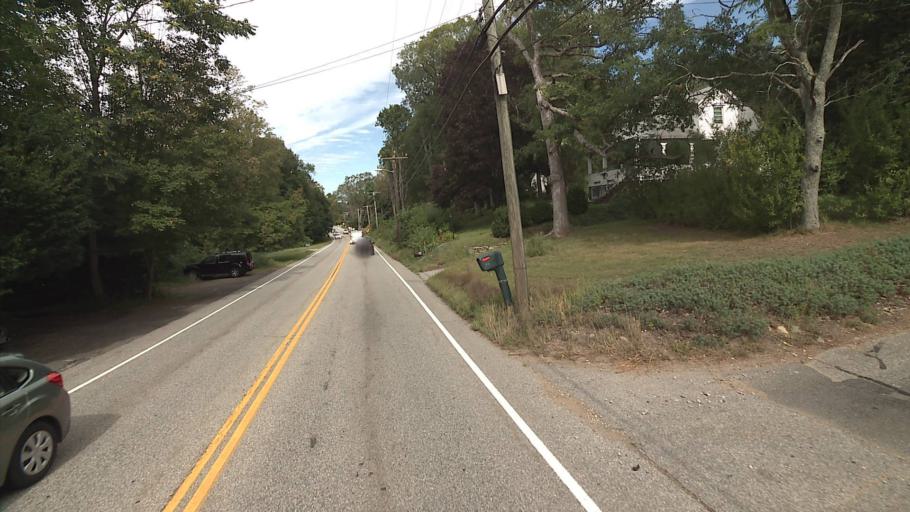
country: US
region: Connecticut
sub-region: Tolland County
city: Mansfield City
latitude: 41.7326
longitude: -72.2506
